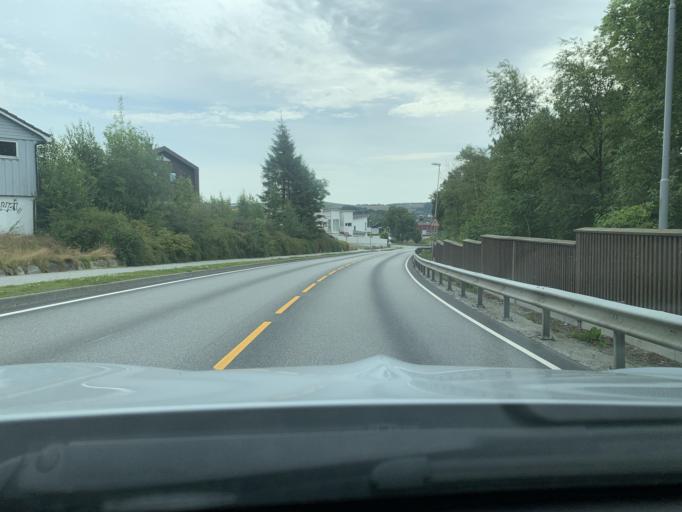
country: NO
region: Rogaland
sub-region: Sandnes
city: Sandnes
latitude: 58.7840
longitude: 5.7126
